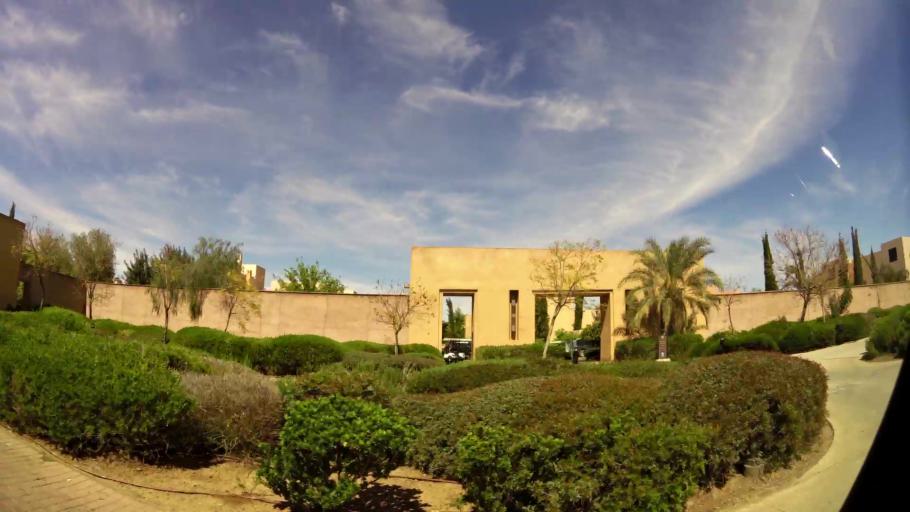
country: MA
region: Marrakech-Tensift-Al Haouz
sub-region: Marrakech
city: Marrakesh
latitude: 31.6006
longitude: -7.9499
